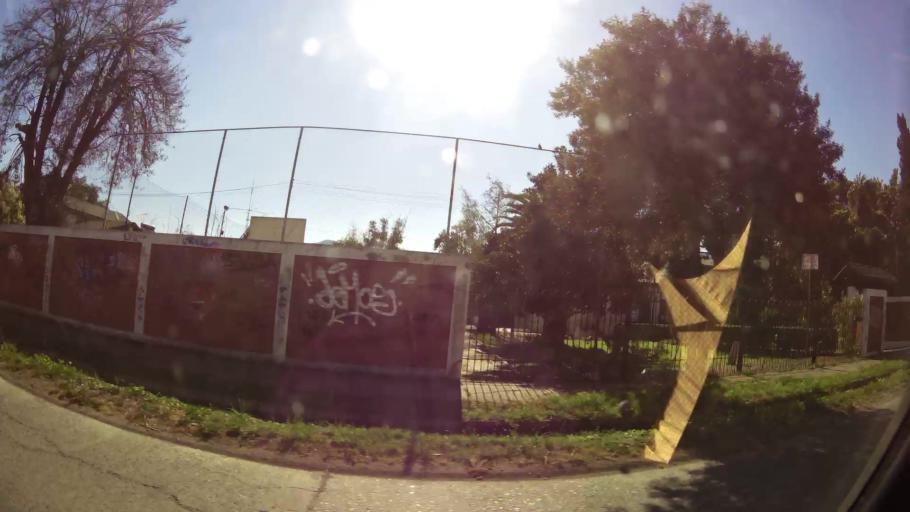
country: CL
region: Santiago Metropolitan
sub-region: Provincia de Talagante
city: Penaflor
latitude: -33.6038
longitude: -70.8980
